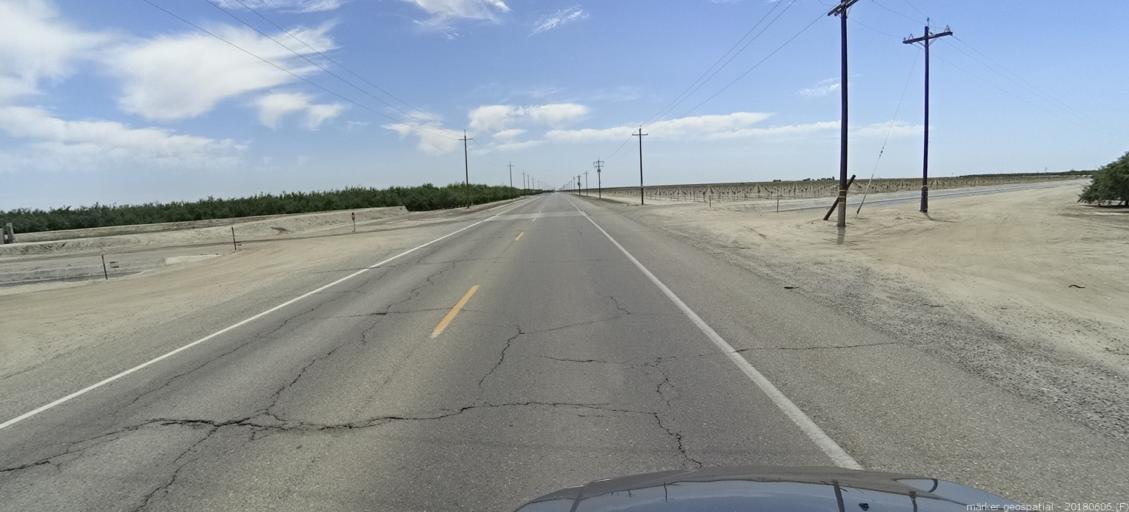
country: US
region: California
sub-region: Fresno County
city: Firebaugh
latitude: 36.8586
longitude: -120.3859
